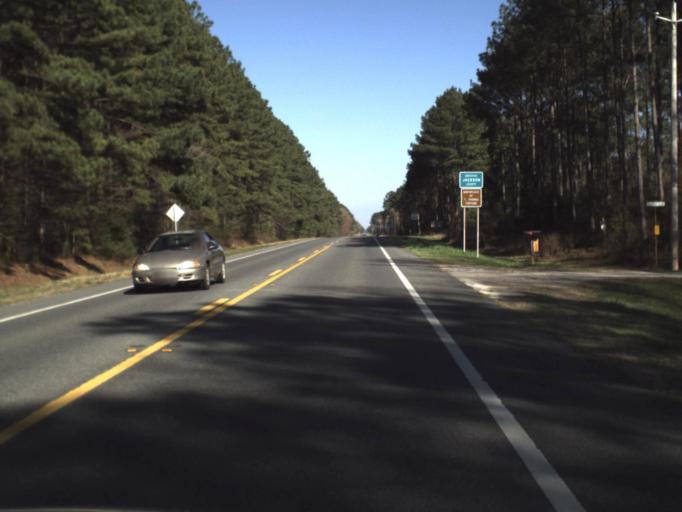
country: US
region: Florida
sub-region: Washington County
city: Chipley
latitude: 30.7858
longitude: -85.4537
